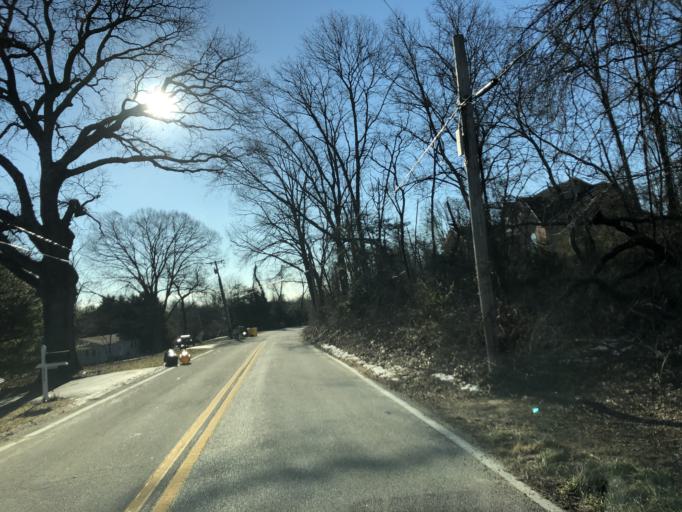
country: US
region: Maryland
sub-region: Anne Arundel County
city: Pasadena
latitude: 39.1249
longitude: -76.5722
